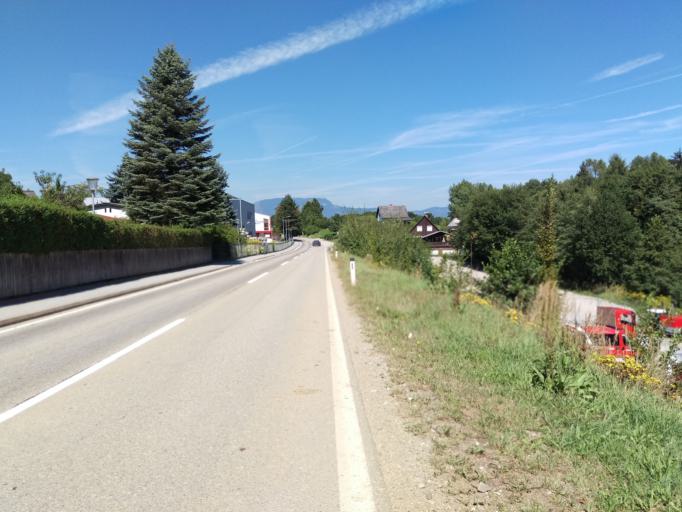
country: AT
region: Styria
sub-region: Politischer Bezirk Graz-Umgebung
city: Eggersdorf bei Graz
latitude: 47.0885
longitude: 15.5748
